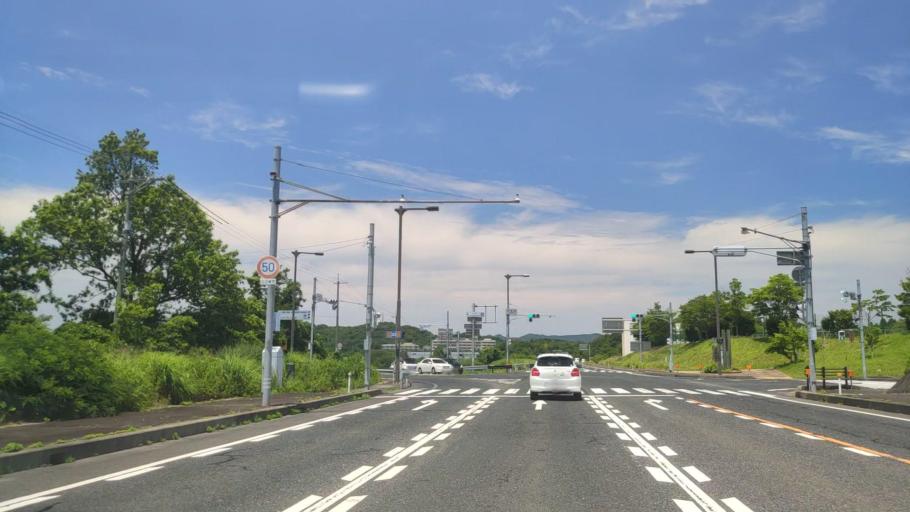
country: JP
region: Tottori
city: Tottori
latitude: 35.4421
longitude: 134.2557
